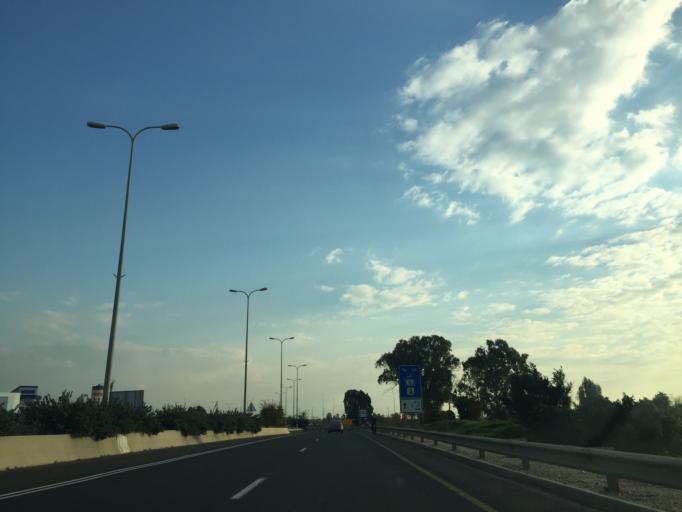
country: IL
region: Central District
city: Ramla
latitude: 31.9206
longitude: 34.8852
